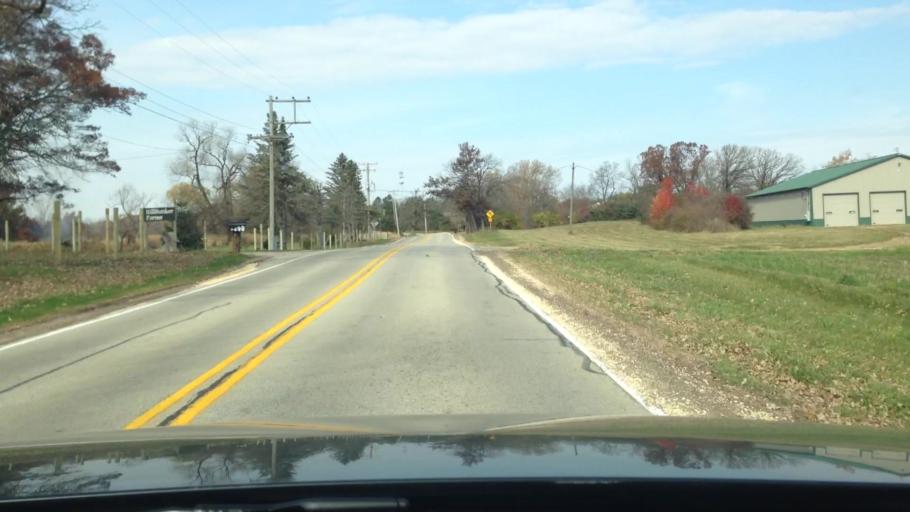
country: US
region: Illinois
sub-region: McHenry County
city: Woodstock
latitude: 42.2567
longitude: -88.4471
